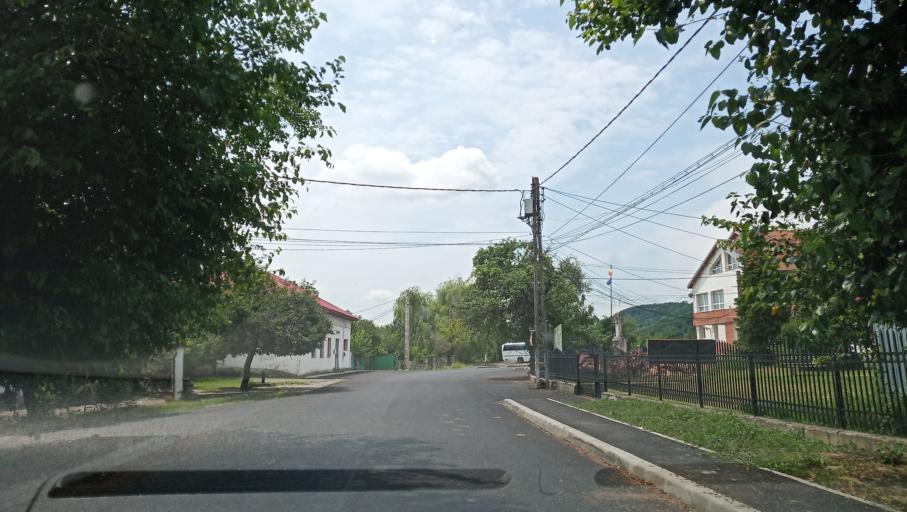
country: RO
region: Gorj
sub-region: Comuna Turcinesti
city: Turcinesti
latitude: 45.1358
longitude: 23.3395
